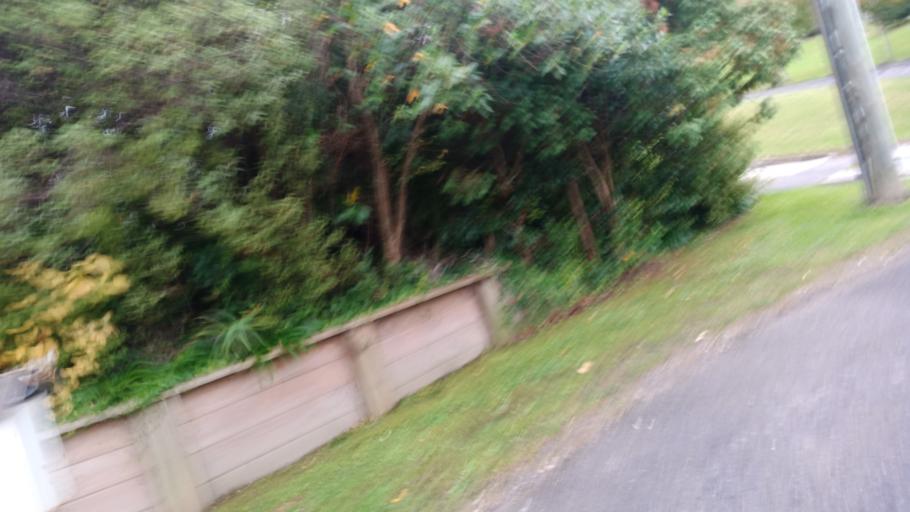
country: NZ
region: Gisborne
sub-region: Gisborne District
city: Gisborne
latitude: -38.6515
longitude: 178.0314
